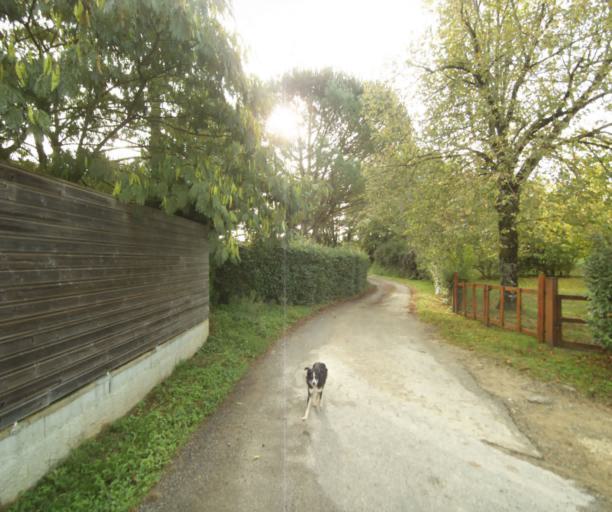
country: FR
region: Midi-Pyrenees
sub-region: Departement du Gers
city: Nogaro
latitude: 43.8179
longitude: -0.0616
